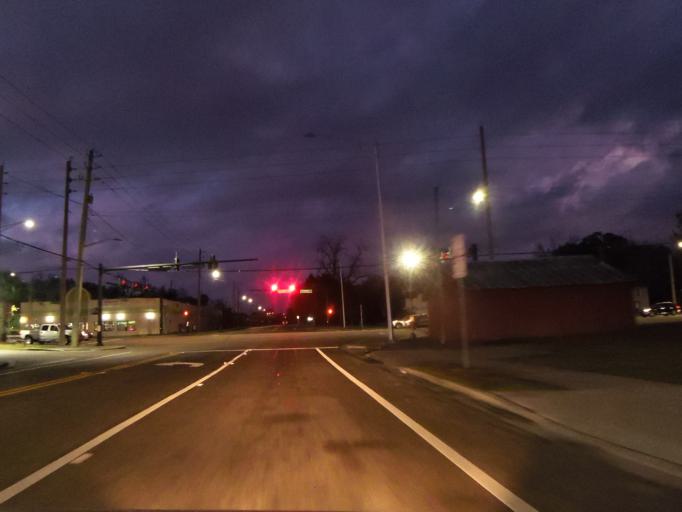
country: US
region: Florida
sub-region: Clay County
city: Bellair-Meadowbrook Terrace
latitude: 30.2480
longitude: -81.7389
